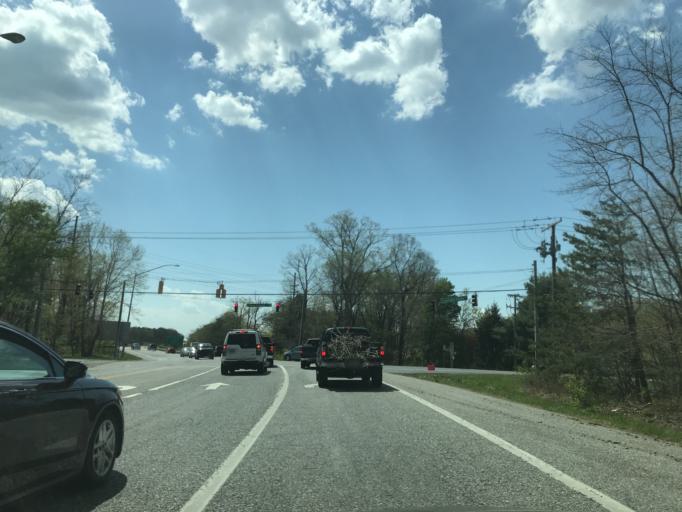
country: US
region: Maryland
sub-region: Anne Arundel County
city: Gambrills
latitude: 39.0817
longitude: -76.6750
